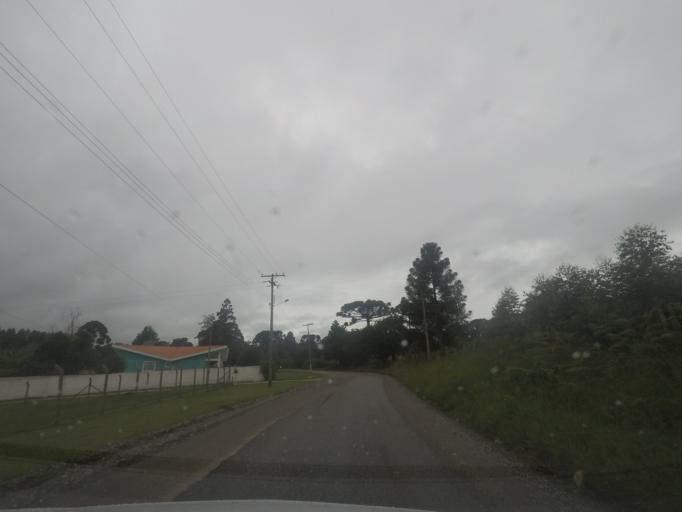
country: BR
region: Parana
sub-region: Campina Grande Do Sul
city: Campina Grande do Sul
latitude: -25.3110
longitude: -49.0900
